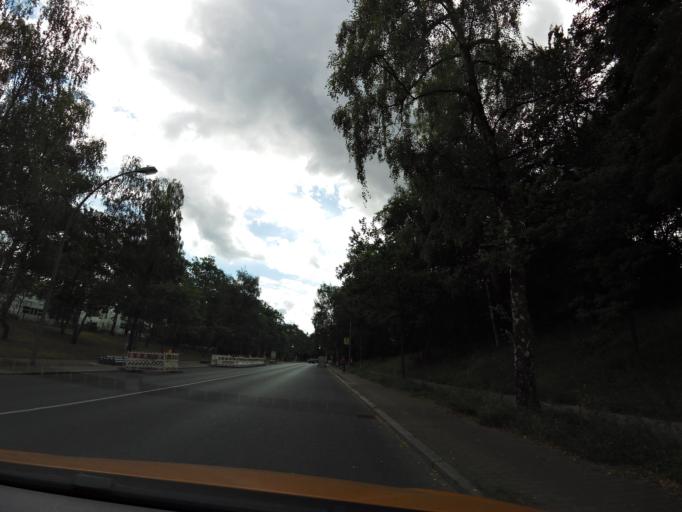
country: DE
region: Berlin
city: Zehlendorf Bezirk
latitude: 52.4253
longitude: 13.2614
